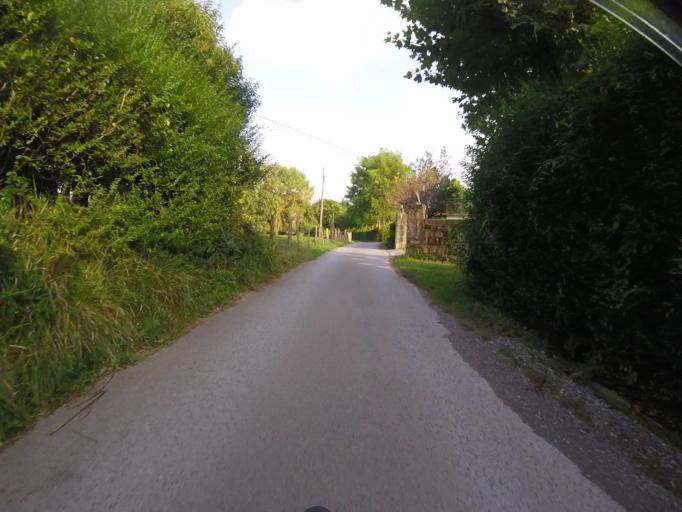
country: ES
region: Basque Country
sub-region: Provincia de Guipuzcoa
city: Fuenterrabia
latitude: 43.3601
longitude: -1.8133
